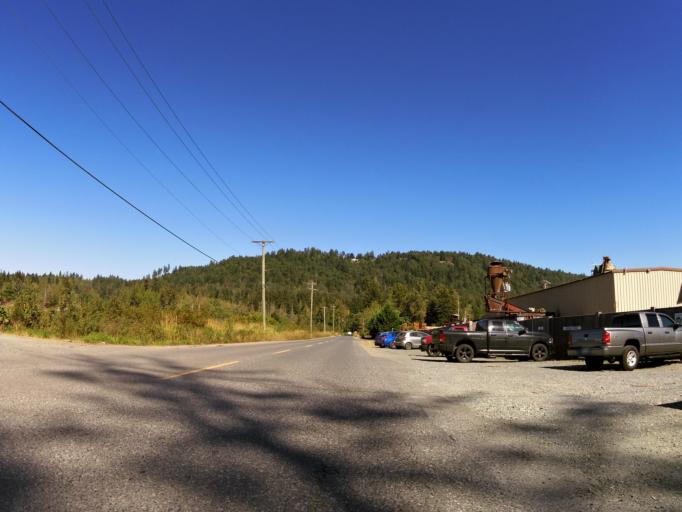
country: CA
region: British Columbia
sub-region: Cowichan Valley Regional District
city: Ladysmith
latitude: 49.0277
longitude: -123.8565
